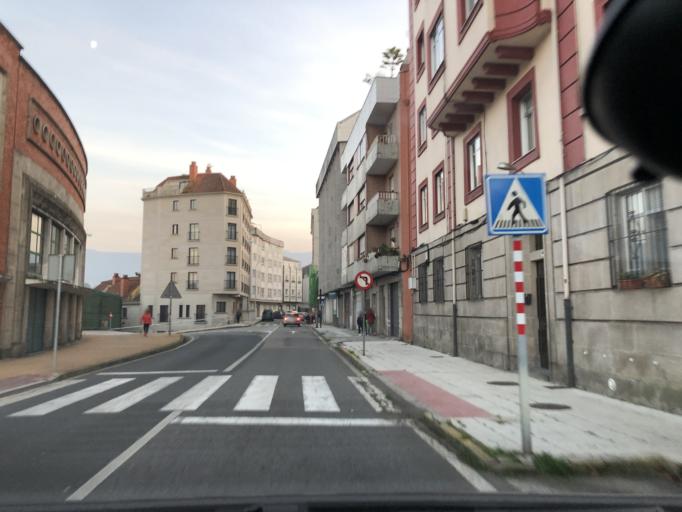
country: ES
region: Galicia
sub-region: Provincia de Pontevedra
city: Marin
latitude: 42.3936
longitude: -8.7067
